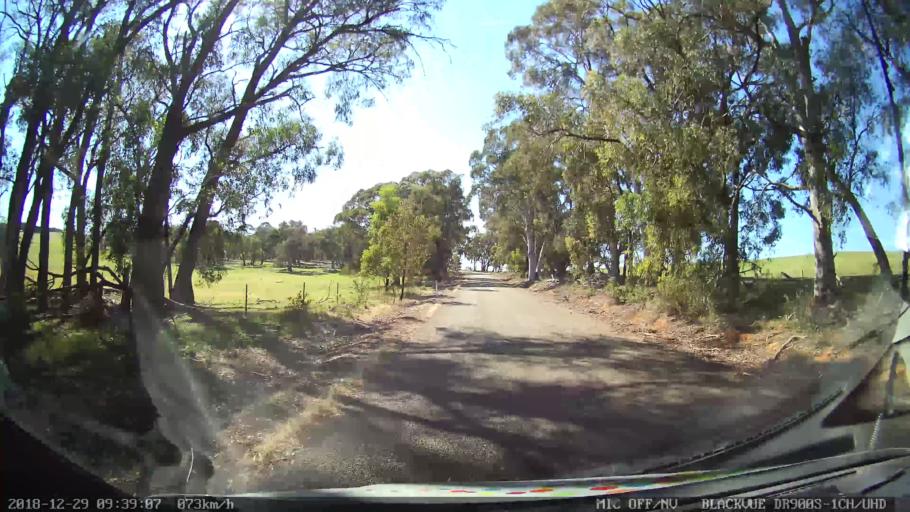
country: AU
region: New South Wales
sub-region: Upper Lachlan Shire
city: Crookwell
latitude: -34.6523
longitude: 149.3820
